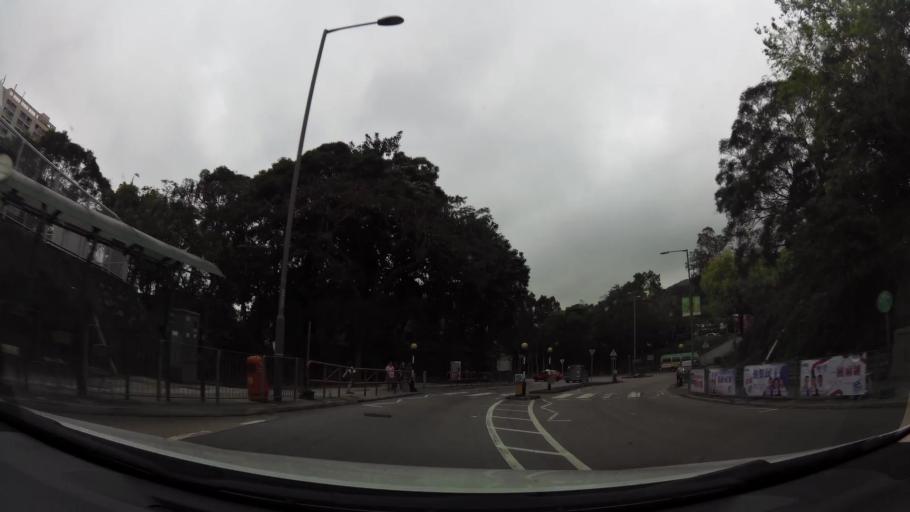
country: HK
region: Tsuen Wan
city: Tsuen Wan
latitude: 22.3796
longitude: 114.1293
